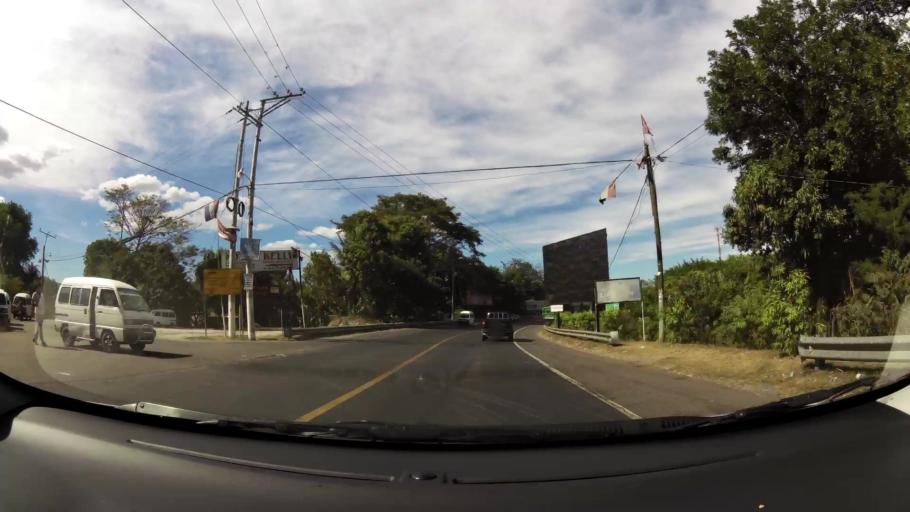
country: SV
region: San Salvador
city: Aguilares
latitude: 13.9411
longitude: -89.1896
